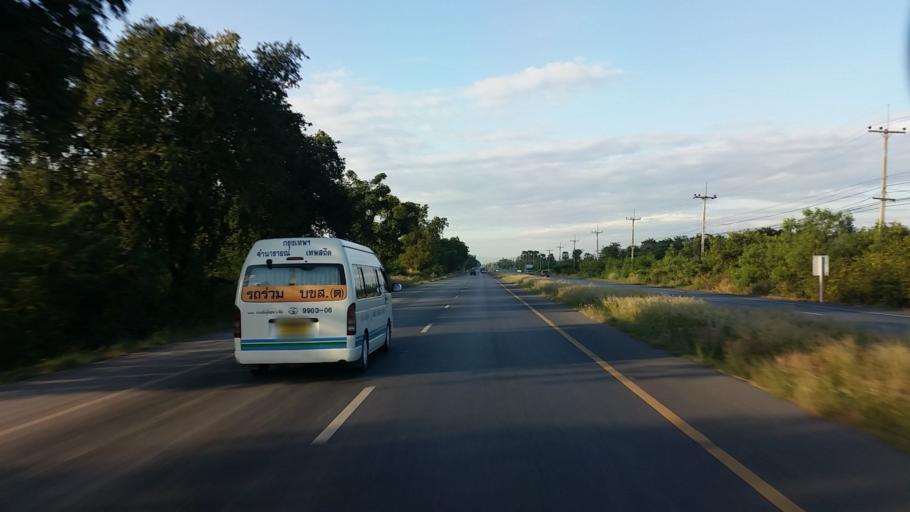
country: TH
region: Lop Buri
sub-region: Amphoe Tha Luang
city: Tha Luang
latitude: 15.0701
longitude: 100.9858
